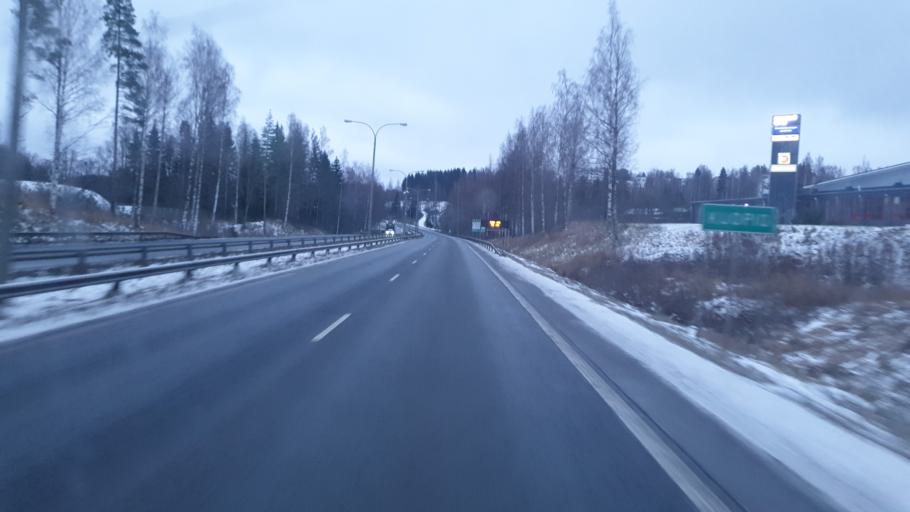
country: FI
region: Northern Savo
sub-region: Kuopio
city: Kuopio
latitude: 62.9198
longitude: 27.6770
